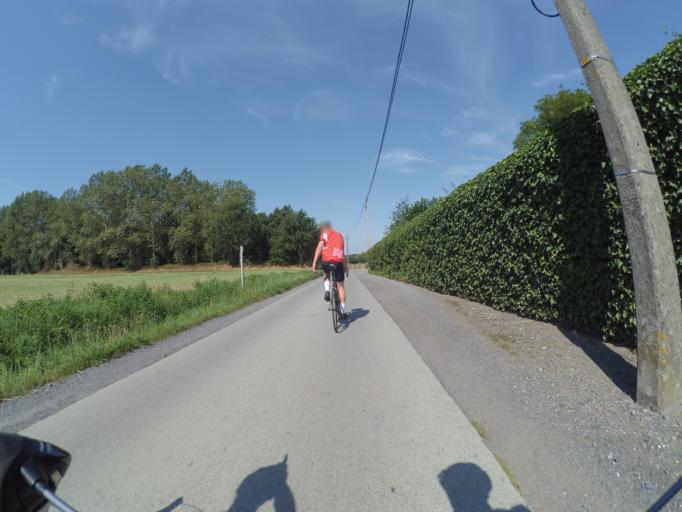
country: BE
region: Flanders
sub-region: Provincie West-Vlaanderen
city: Anzegem
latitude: 50.8701
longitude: 3.4774
